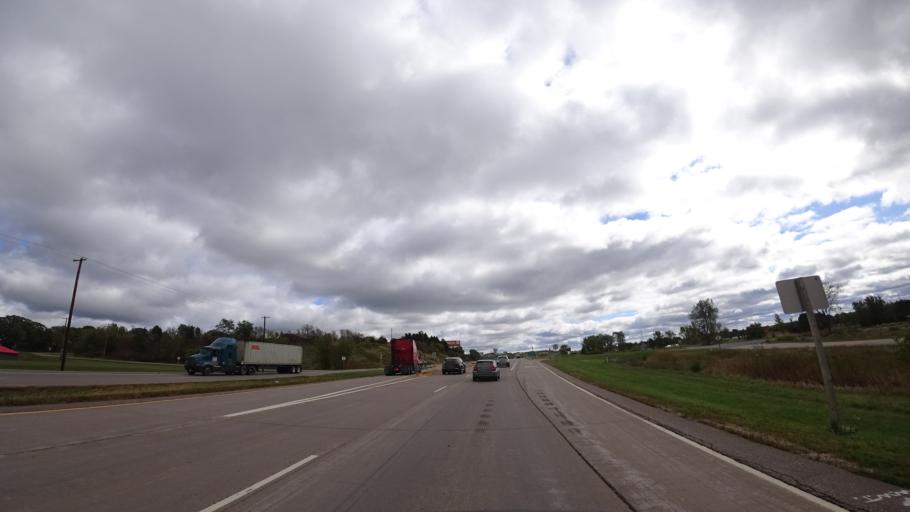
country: US
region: Wisconsin
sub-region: Eau Claire County
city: Eau Claire
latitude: 44.8427
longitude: -91.5570
